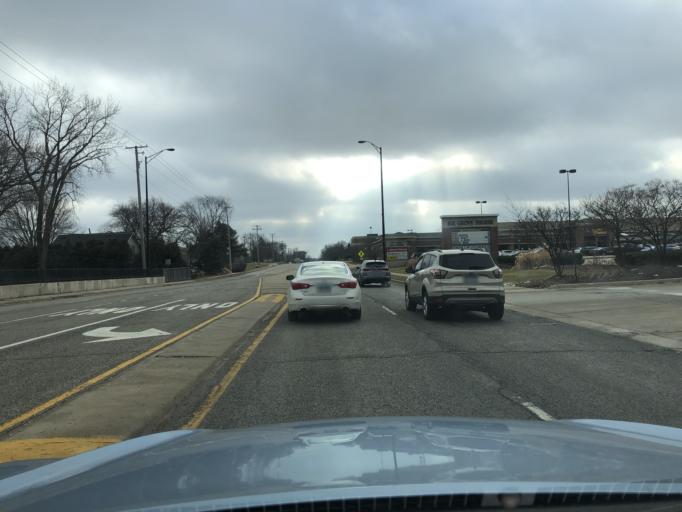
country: US
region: Illinois
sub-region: DuPage County
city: Itasca
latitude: 42.0029
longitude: -88.0037
